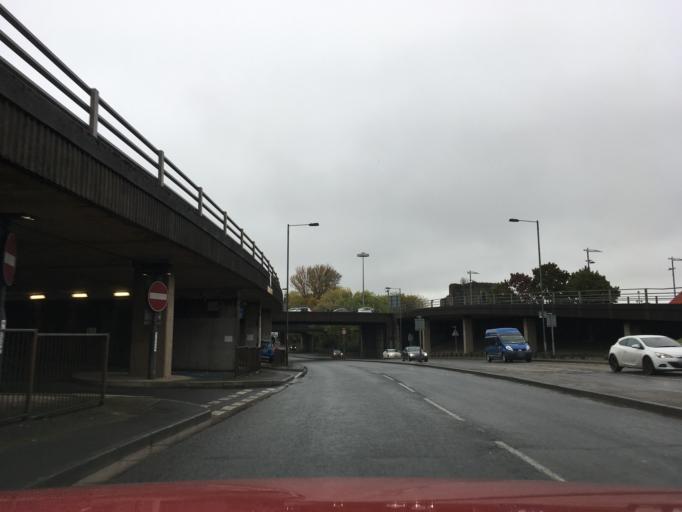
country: GB
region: Wales
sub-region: Newport
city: Newport
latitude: 51.5889
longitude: -2.9947
